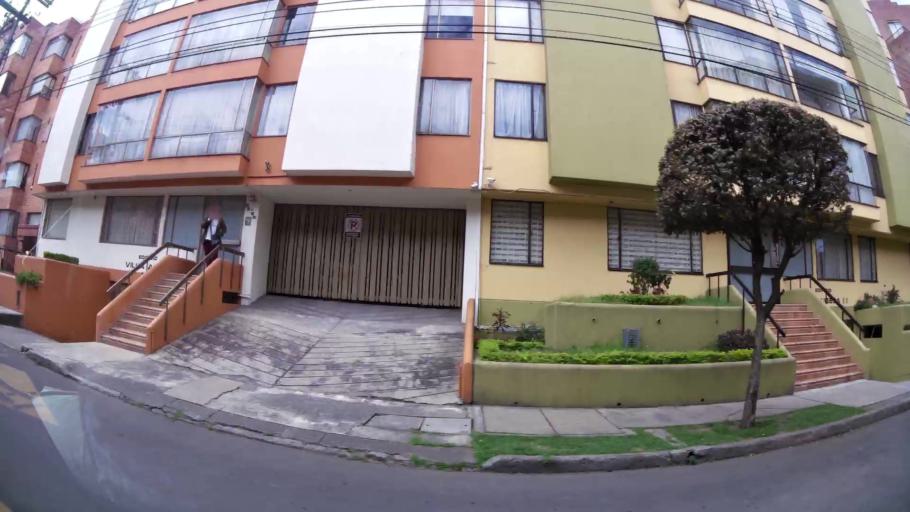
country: CO
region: Bogota D.C.
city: Bogota
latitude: 4.6341
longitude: -74.0965
